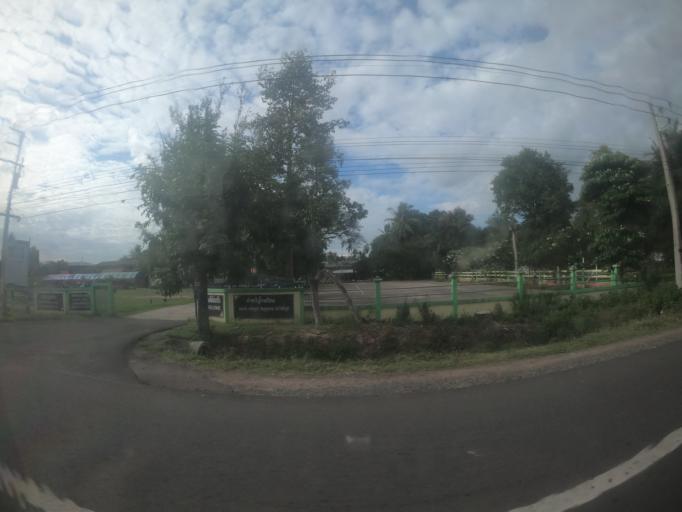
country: TH
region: Surin
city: Prasat
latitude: 14.5911
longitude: 103.4548
